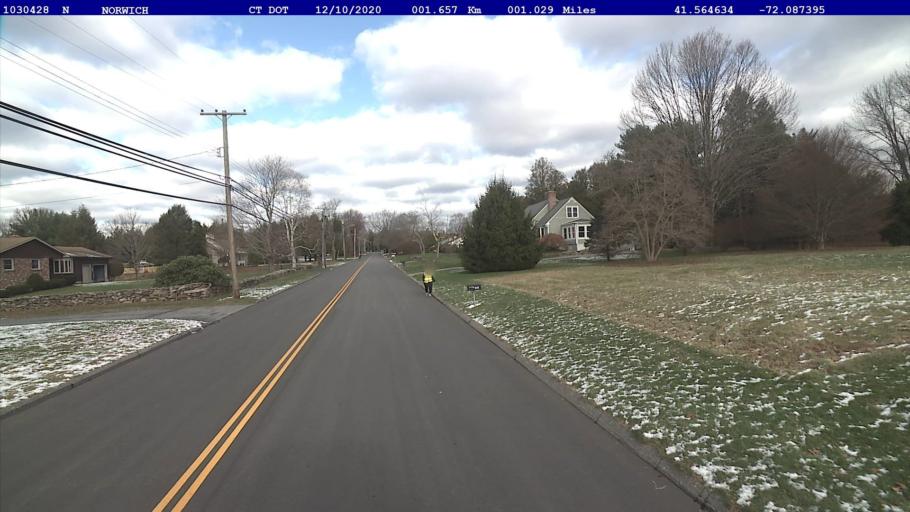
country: US
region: Connecticut
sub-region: New London County
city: Norwich
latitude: 41.5646
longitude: -72.0874
